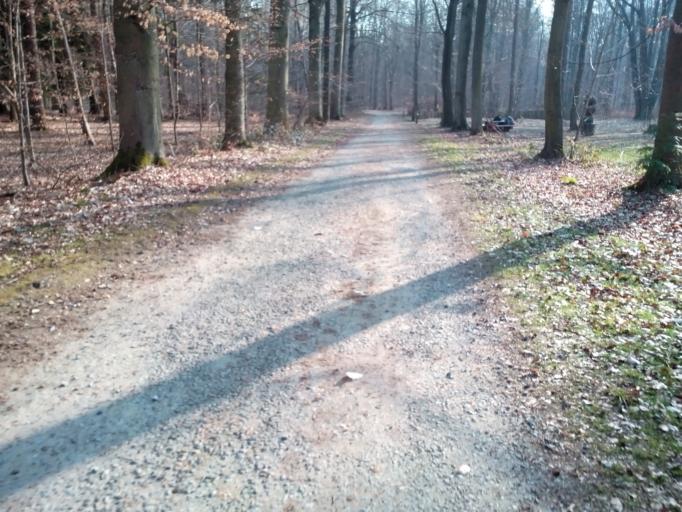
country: BE
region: Flanders
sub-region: Provincie Vlaams-Brabant
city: Oud-Heverlee
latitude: 50.8412
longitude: 4.6925
